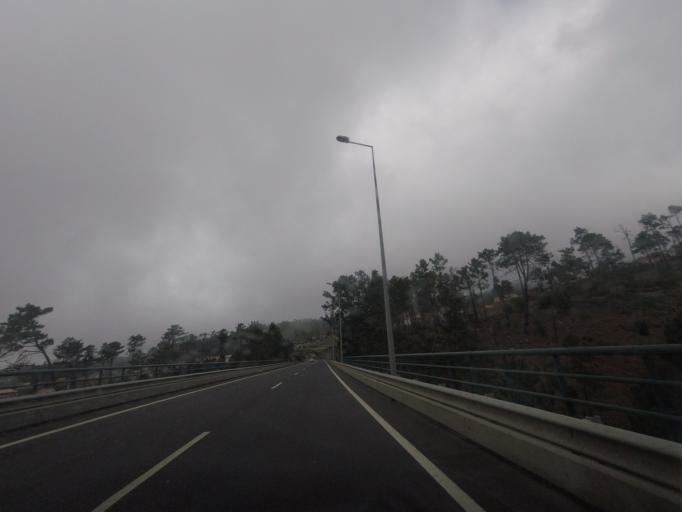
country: PT
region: Madeira
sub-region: Calheta
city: Faja da Ovelha
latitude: 32.7618
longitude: -17.2058
